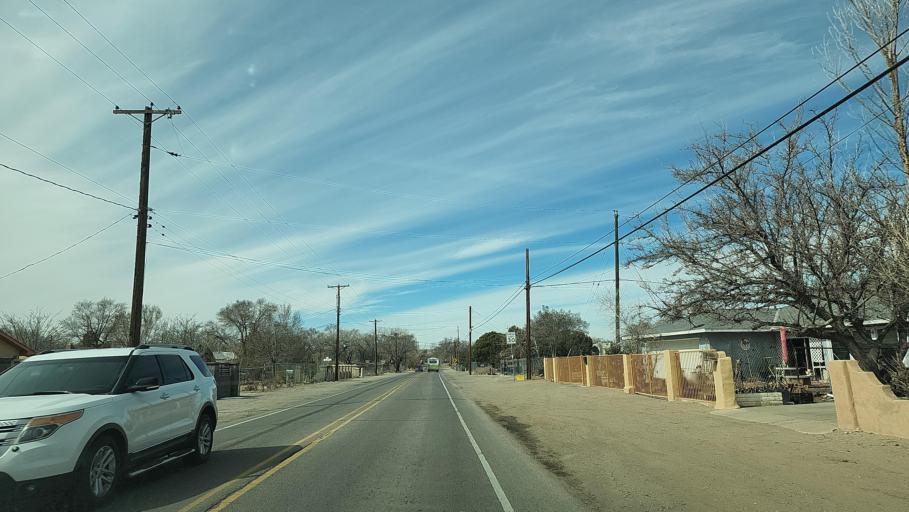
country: US
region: New Mexico
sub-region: Bernalillo County
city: South Valley
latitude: 35.0364
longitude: -106.6881
